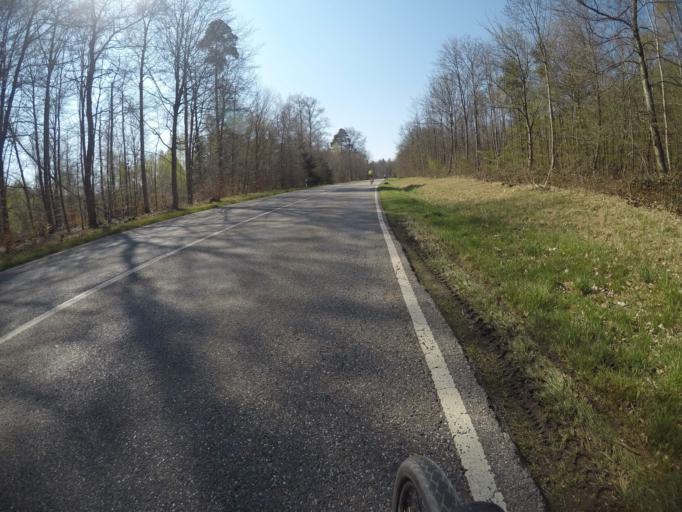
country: DE
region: Baden-Wuerttemberg
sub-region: Regierungsbezirk Stuttgart
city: Leonberg
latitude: 48.7543
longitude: 9.0382
